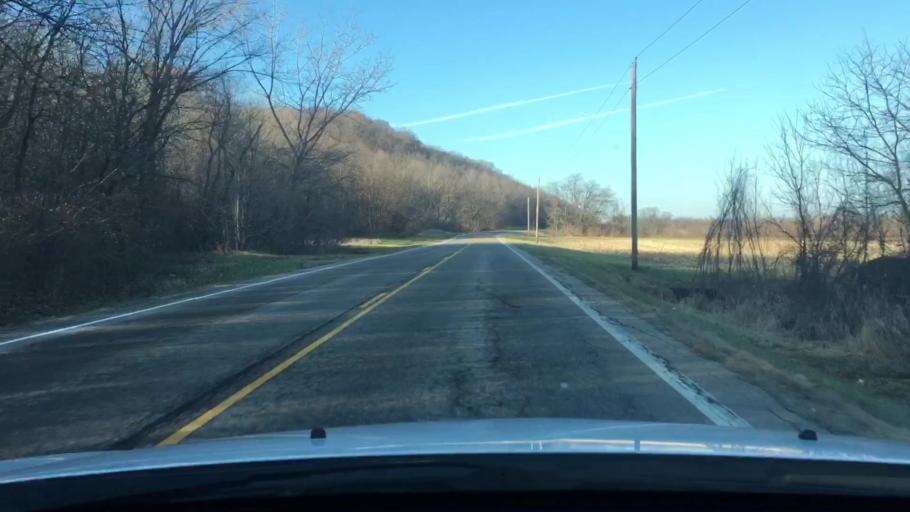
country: US
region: Illinois
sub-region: Bureau County
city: Spring Valley
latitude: 41.3005
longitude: -89.1765
